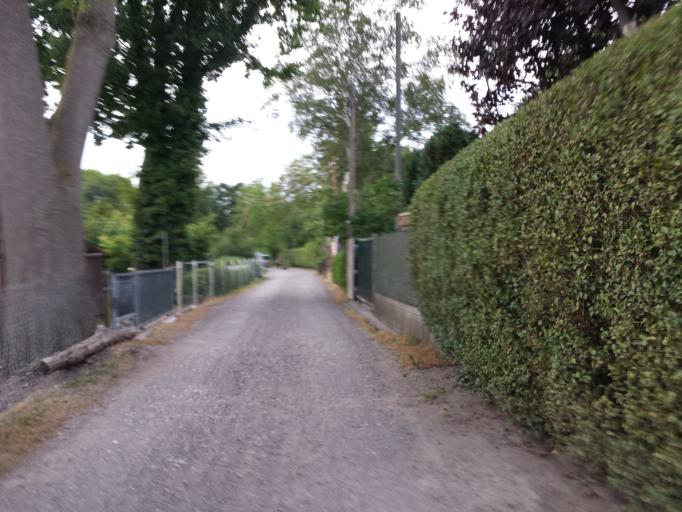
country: DE
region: Lower Saxony
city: Stuhr
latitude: 53.0681
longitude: 8.7620
